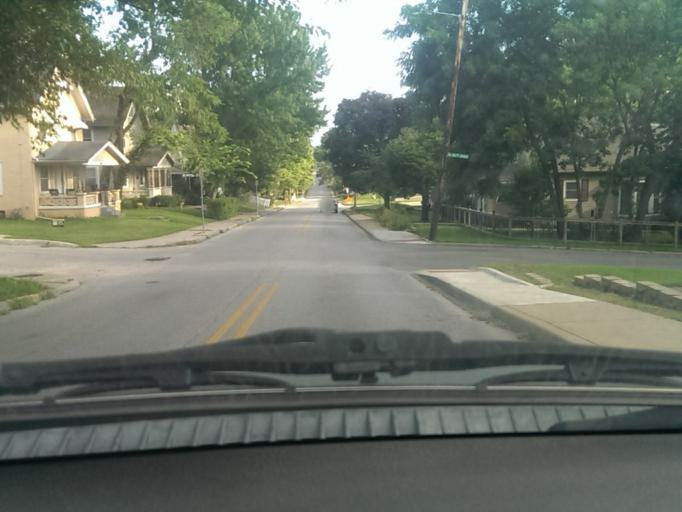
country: US
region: Kansas
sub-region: Johnson County
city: Westwood
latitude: 39.0449
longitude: -94.6074
